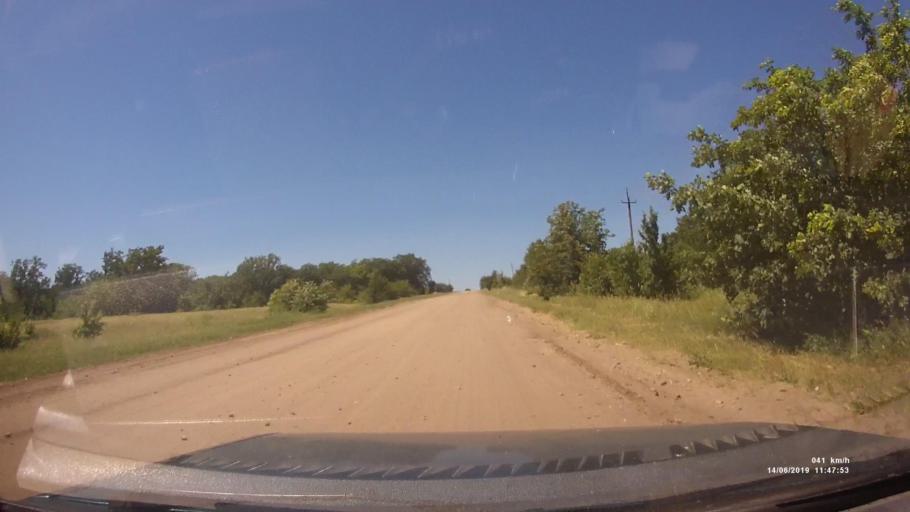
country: RU
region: Rostov
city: Kazanskaya
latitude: 49.8518
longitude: 41.2914
